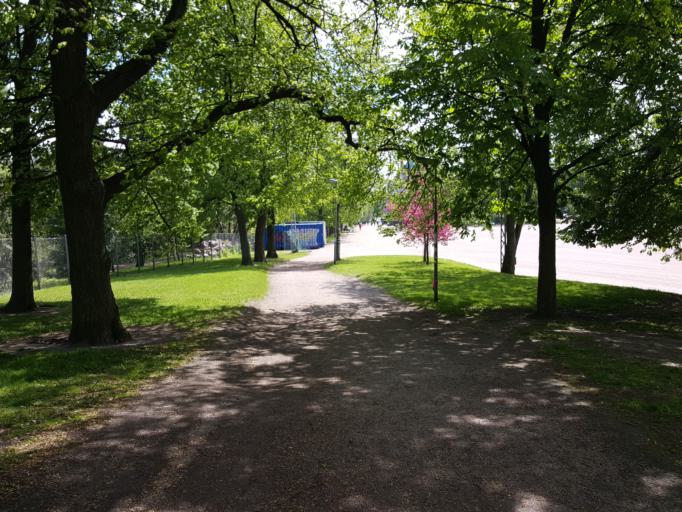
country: FI
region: Uusimaa
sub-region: Helsinki
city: Helsinki
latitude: 60.1759
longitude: 24.9439
